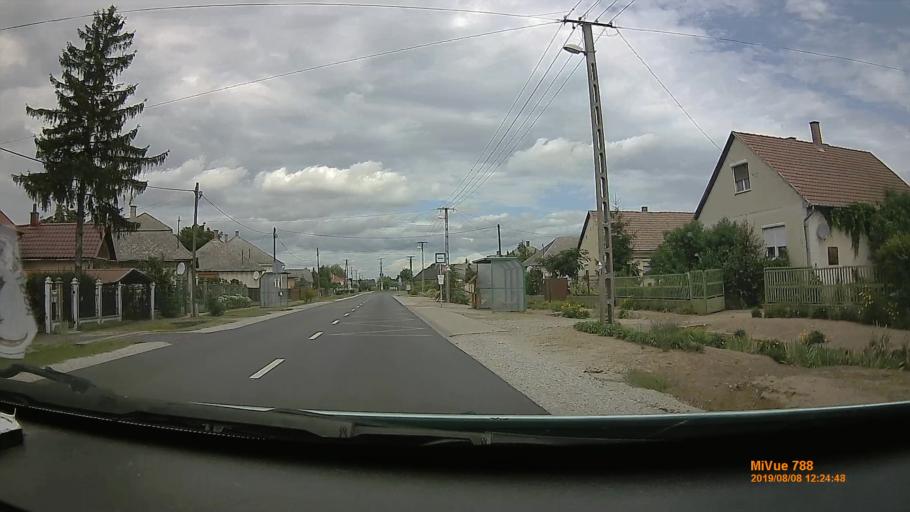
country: HU
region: Szabolcs-Szatmar-Bereg
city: Nyirbogat
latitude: 47.8070
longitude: 22.0661
